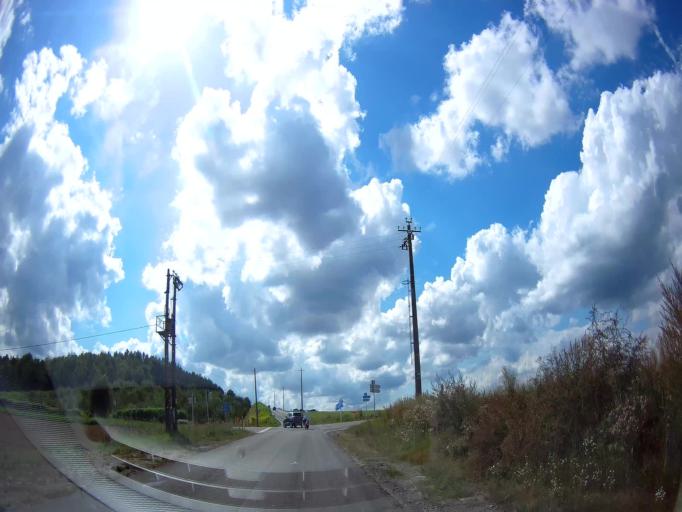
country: BE
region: Wallonia
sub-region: Province de Namur
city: Gesves
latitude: 50.3927
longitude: 5.0912
